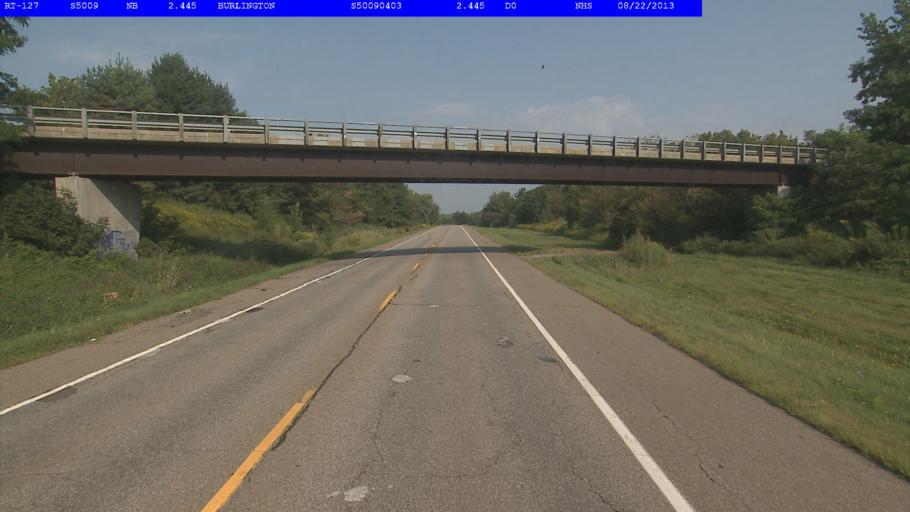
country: US
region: Vermont
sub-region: Chittenden County
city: Burlington
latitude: 44.5174
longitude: -73.2410
